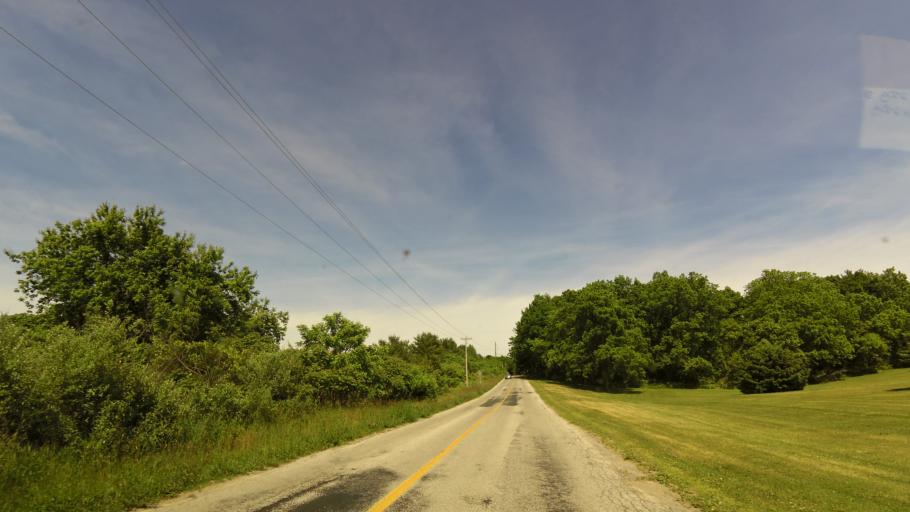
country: CA
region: Ontario
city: Norfolk County
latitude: 42.7199
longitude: -80.3078
